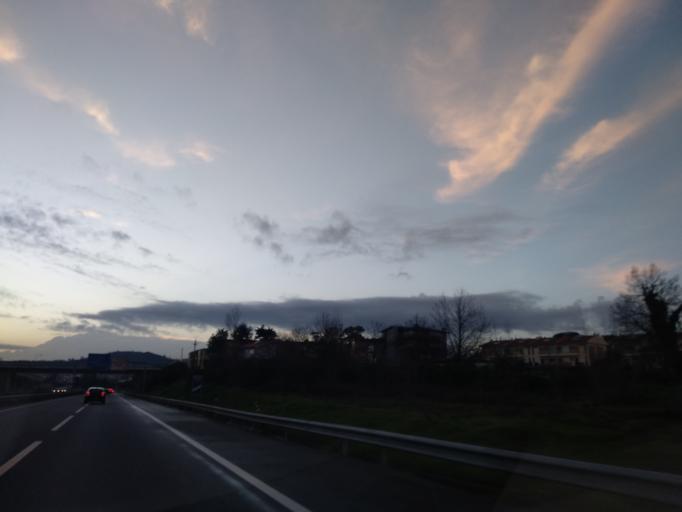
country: PT
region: Braga
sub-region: Vila Nova de Famalicao
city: Vila Nova de Famalicao
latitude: 41.3844
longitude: -8.5106
